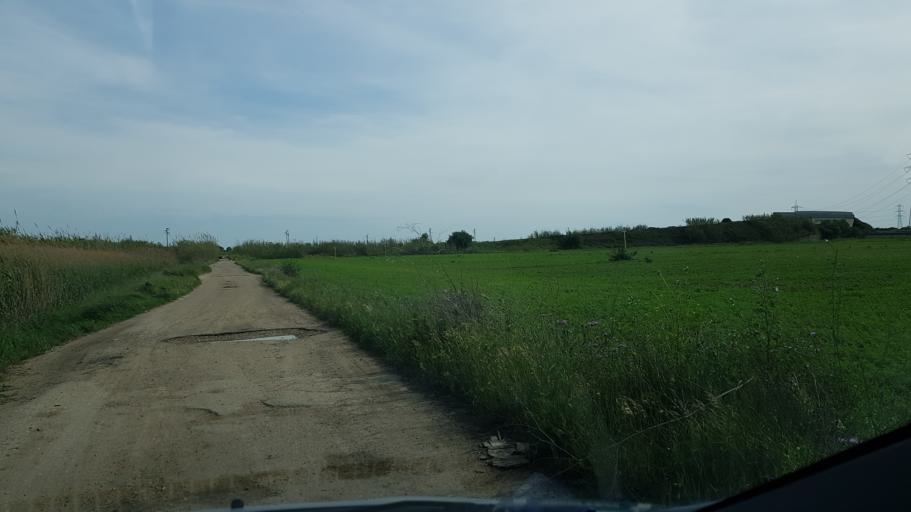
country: IT
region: Apulia
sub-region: Provincia di Brindisi
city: La Rosa
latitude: 40.6018
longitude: 17.9698
